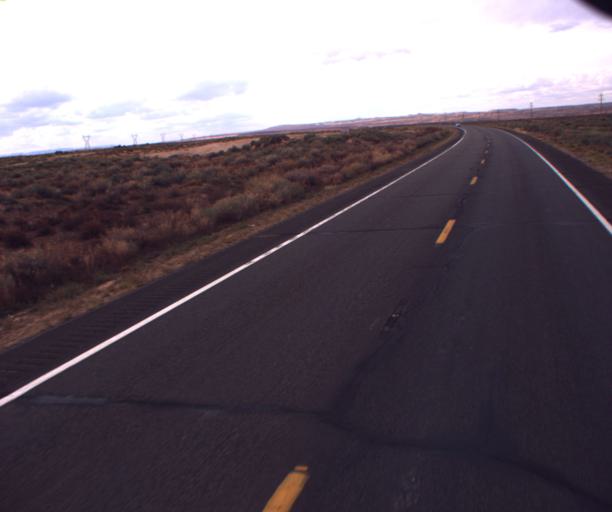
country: US
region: Arizona
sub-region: Apache County
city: Many Farms
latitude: 36.9414
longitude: -109.6466
